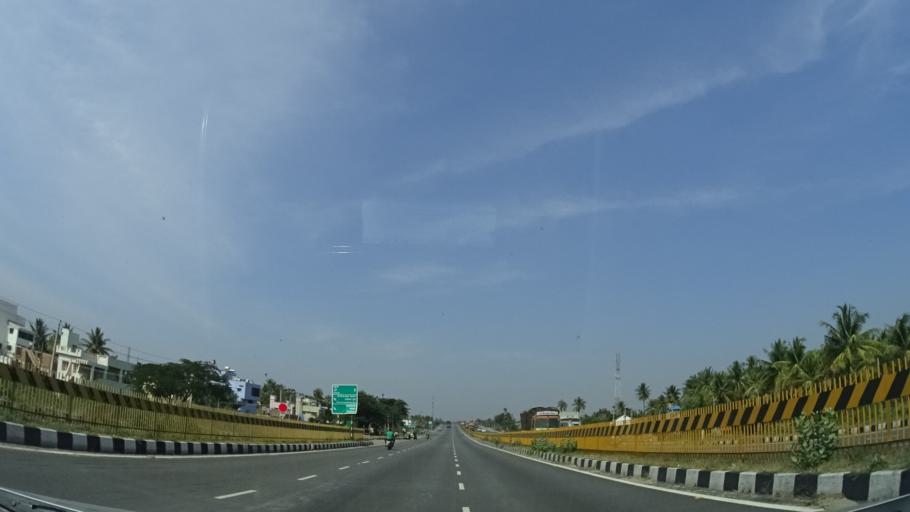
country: IN
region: Karnataka
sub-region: Tumkur
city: Tumkur
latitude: 13.3425
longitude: 77.1267
